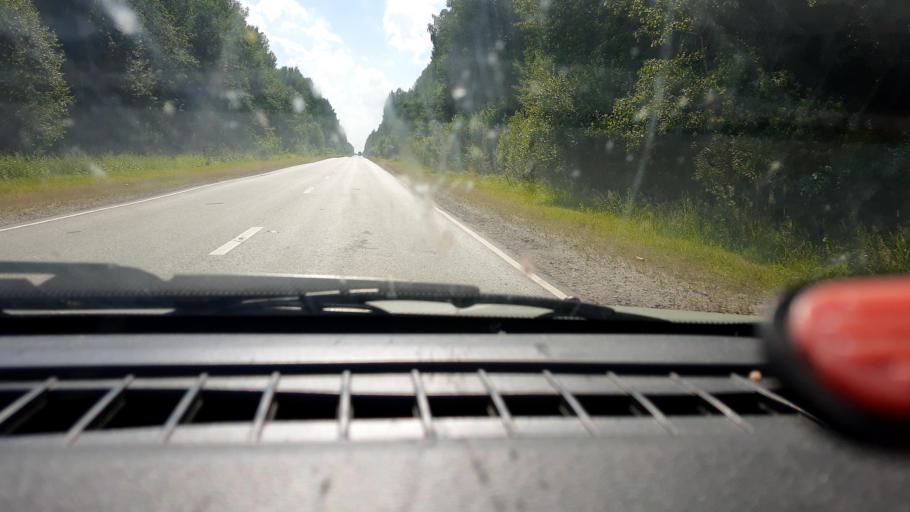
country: RU
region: Nizjnij Novgorod
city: Uren'
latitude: 57.2335
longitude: 45.5518
